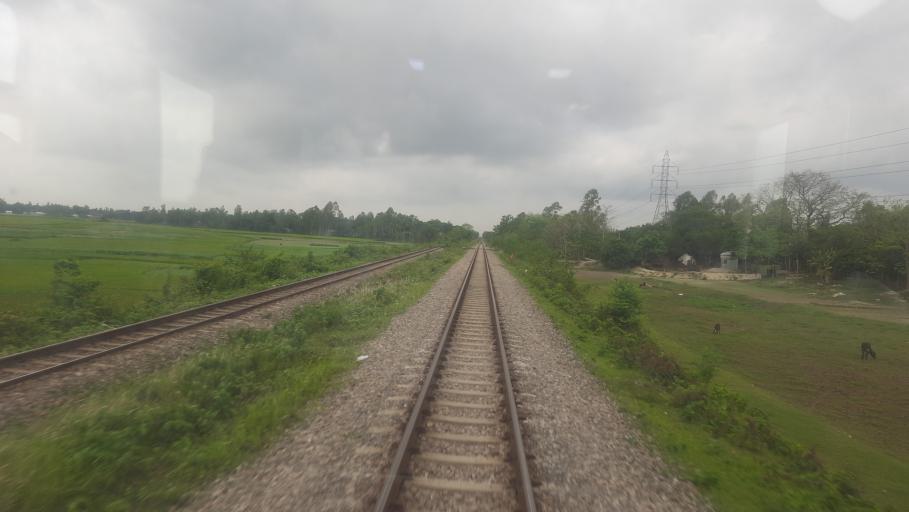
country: BD
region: Dhaka
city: Bhairab Bazar
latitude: 23.9997
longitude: 90.8857
